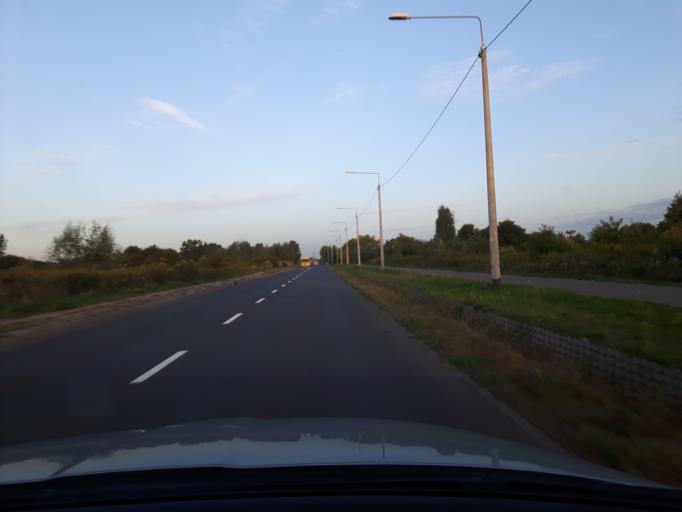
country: PL
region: Masovian Voivodeship
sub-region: Warszawa
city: Wawer
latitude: 52.1847
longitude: 21.1657
